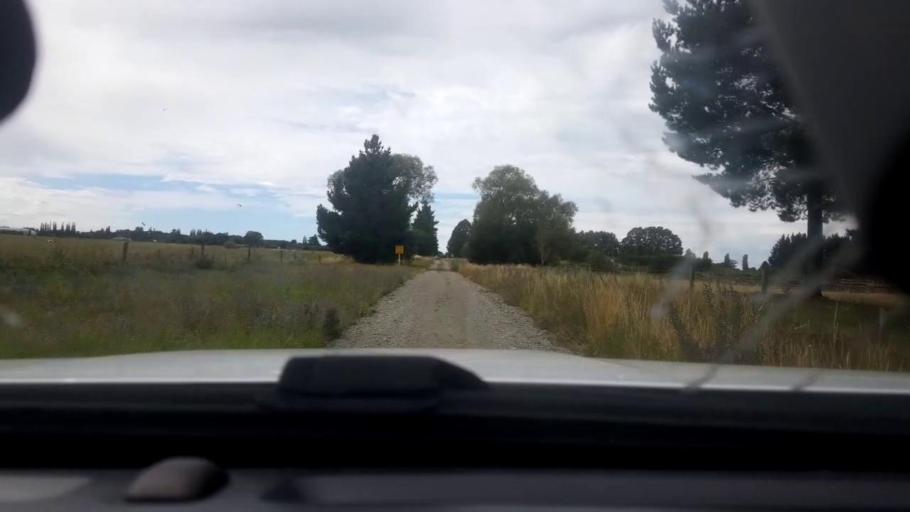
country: NZ
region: Canterbury
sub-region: Timaru District
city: Pleasant Point
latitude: -44.1330
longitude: 171.2835
